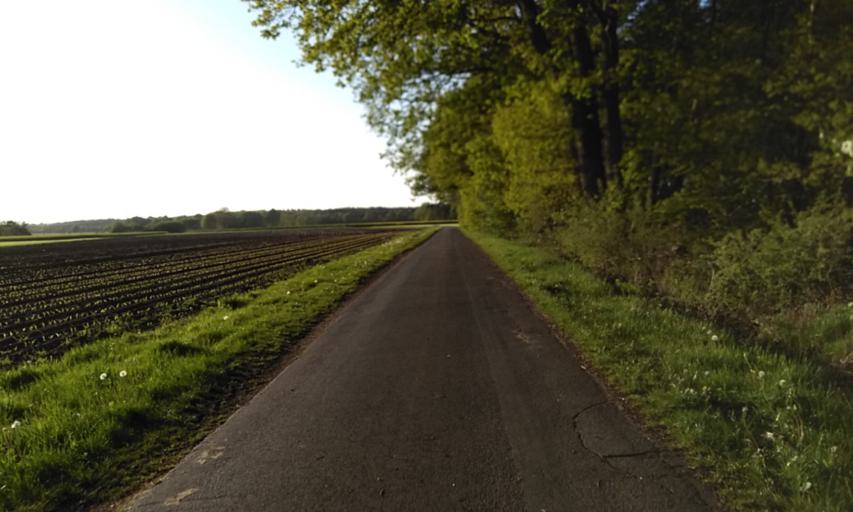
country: DE
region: Lower Saxony
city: Harsefeld
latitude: 53.4060
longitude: 9.5102
